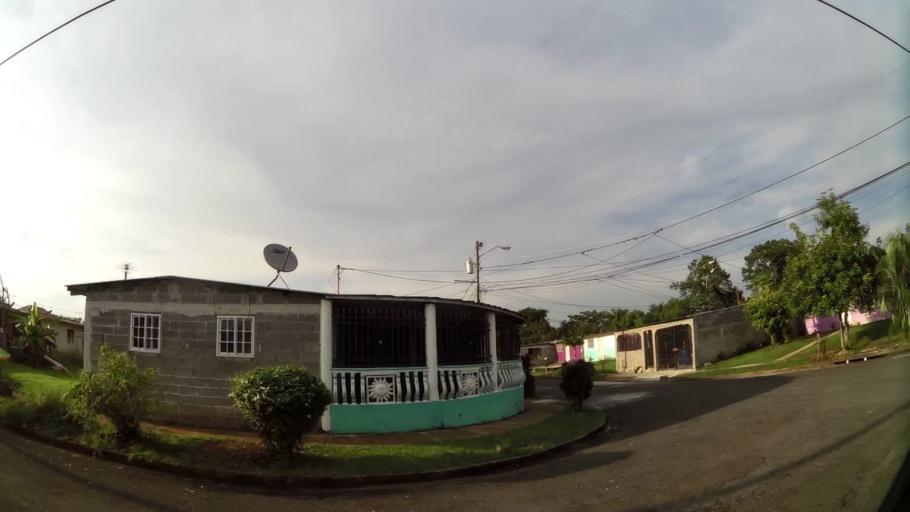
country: PA
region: Panama
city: Tocumen
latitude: 9.0837
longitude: -79.3549
